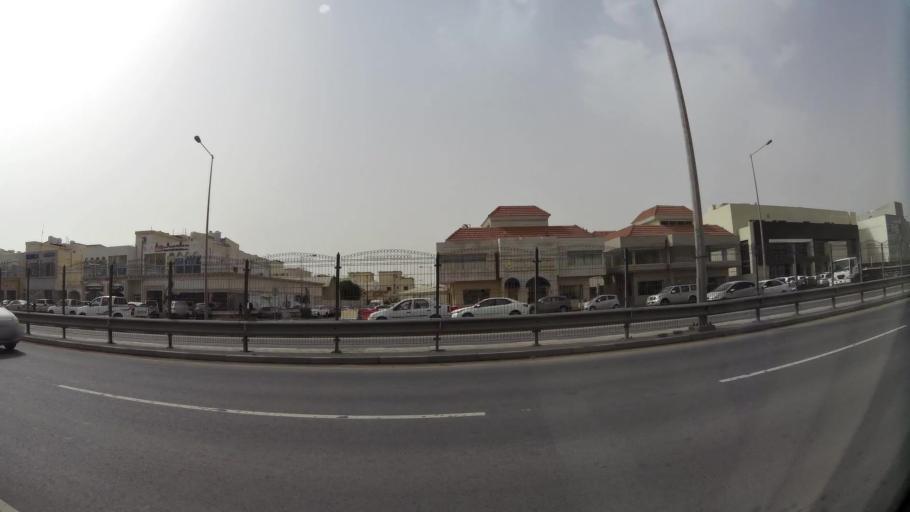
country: QA
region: Baladiyat ad Dawhah
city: Doha
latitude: 25.2630
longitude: 51.5309
